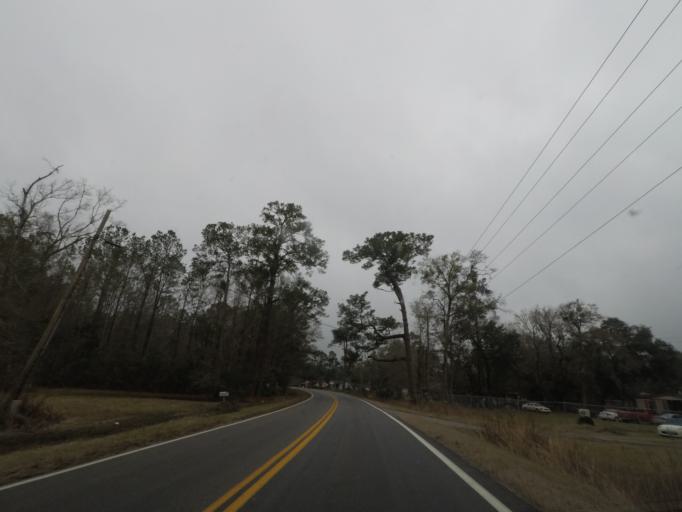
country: US
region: South Carolina
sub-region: Charleston County
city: Ravenel
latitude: 32.7262
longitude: -80.3532
